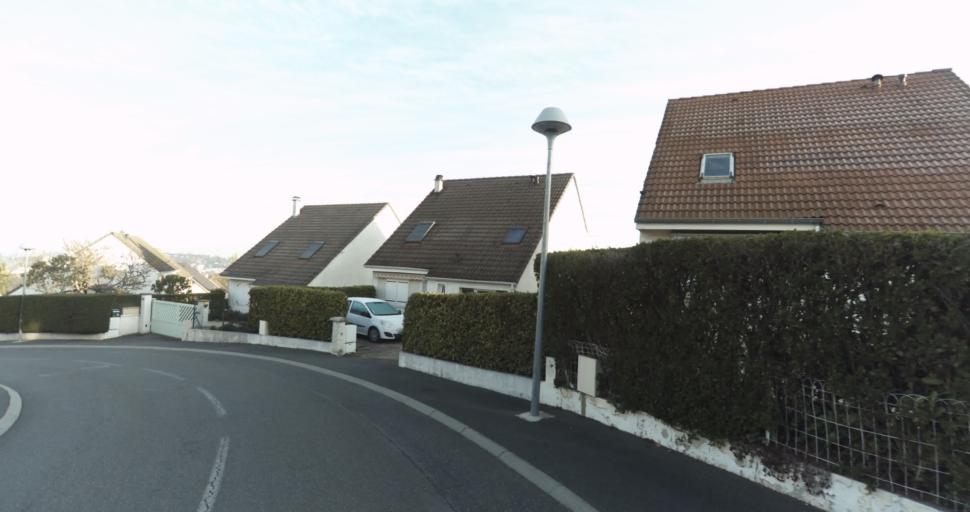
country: FR
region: Rhone-Alpes
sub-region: Departement de la Loire
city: Saint-Jean-Bonnefonds
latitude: 45.4522
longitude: 4.4292
